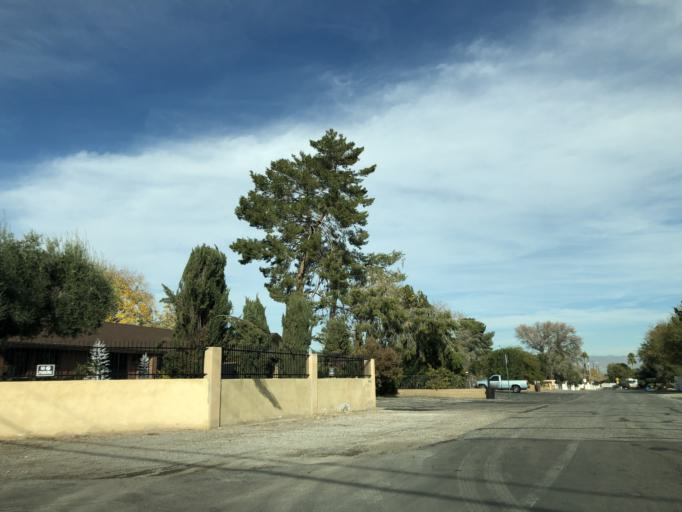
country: US
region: Nevada
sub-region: Clark County
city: Winchester
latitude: 36.1166
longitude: -115.1168
